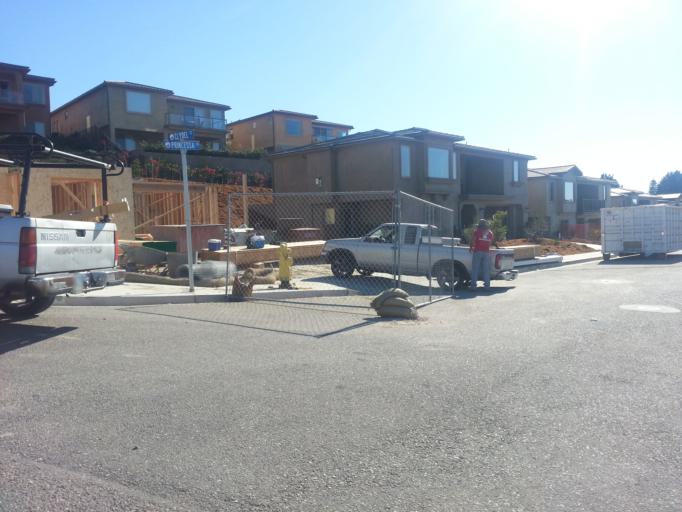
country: US
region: California
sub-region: San Luis Obispo County
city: Pismo Beach
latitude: 35.1452
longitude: -120.6265
